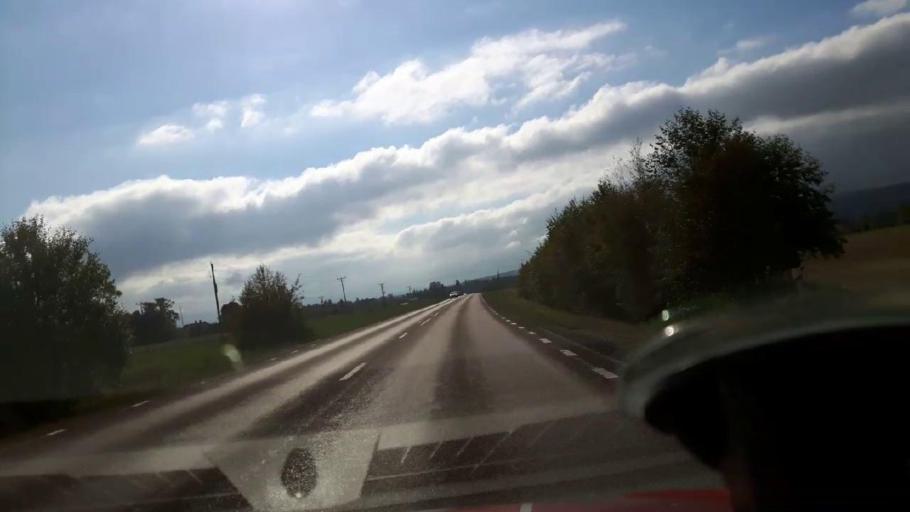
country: SE
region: Gaevleborg
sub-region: Bollnas Kommun
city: Arbra
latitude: 61.5335
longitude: 16.3638
